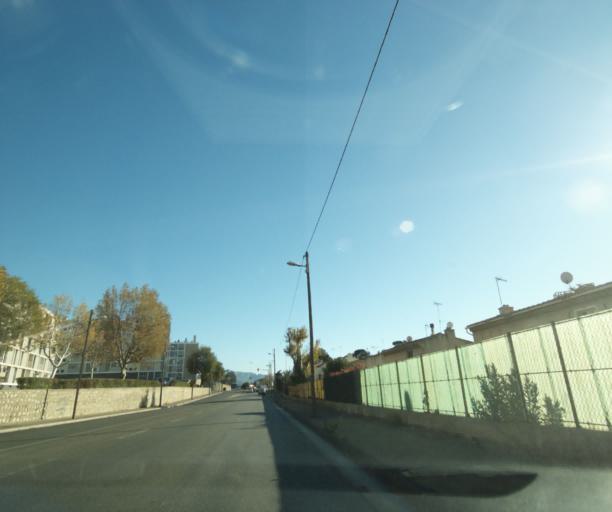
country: FR
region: Provence-Alpes-Cote d'Azur
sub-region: Departement des Bouches-du-Rhone
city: Marseille 14
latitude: 43.3507
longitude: 5.3742
